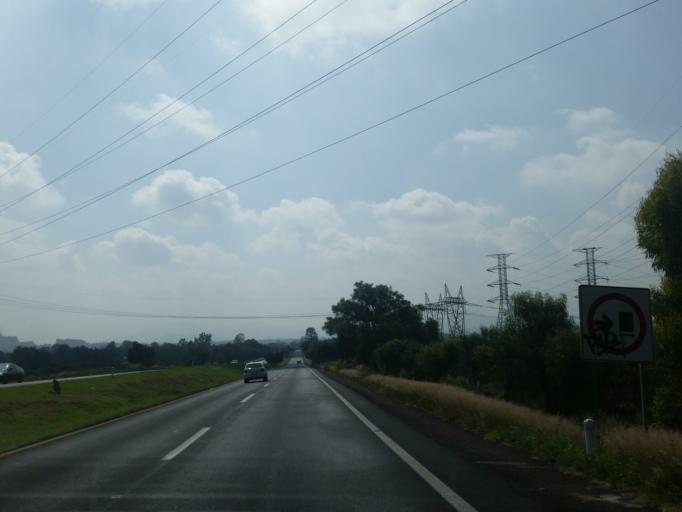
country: MX
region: Mexico
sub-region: Acolman de Nezahualcoyotl
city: Prados de San Juan
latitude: 19.6216
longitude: -98.9766
